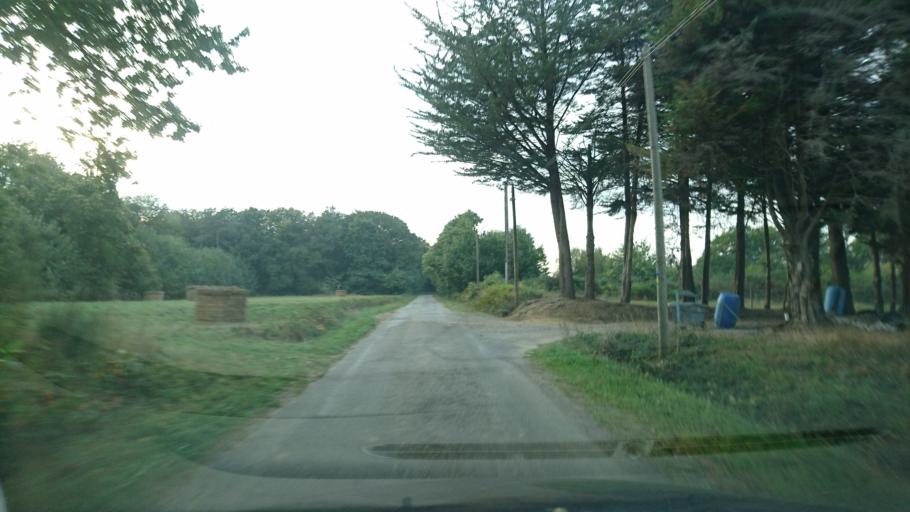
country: FR
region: Brittany
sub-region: Departement du Morbihan
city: Saint-Vincent-sur-Oust
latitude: 47.6943
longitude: -2.1371
